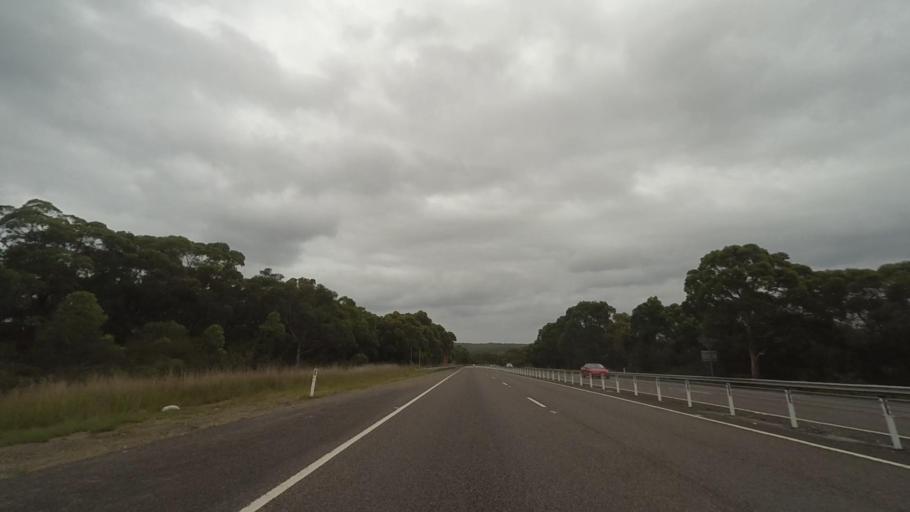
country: AU
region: New South Wales
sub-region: Lake Macquarie Shire
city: Arcadia vale
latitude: -33.1283
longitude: 151.6304
